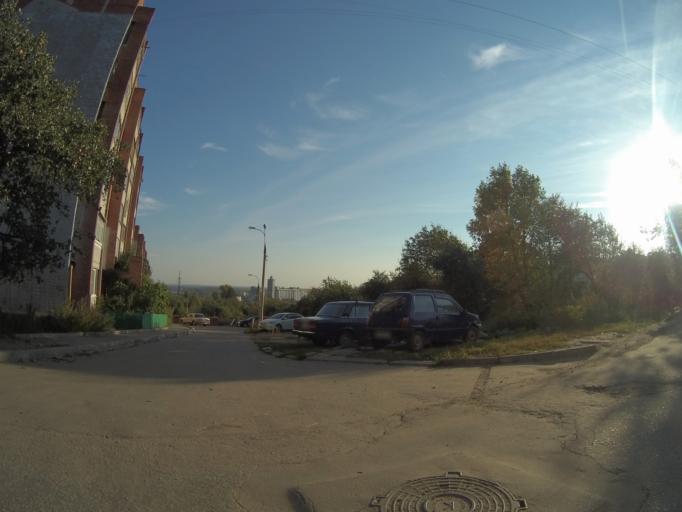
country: RU
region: Vladimir
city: Vladimir
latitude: 56.1088
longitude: 40.3727
